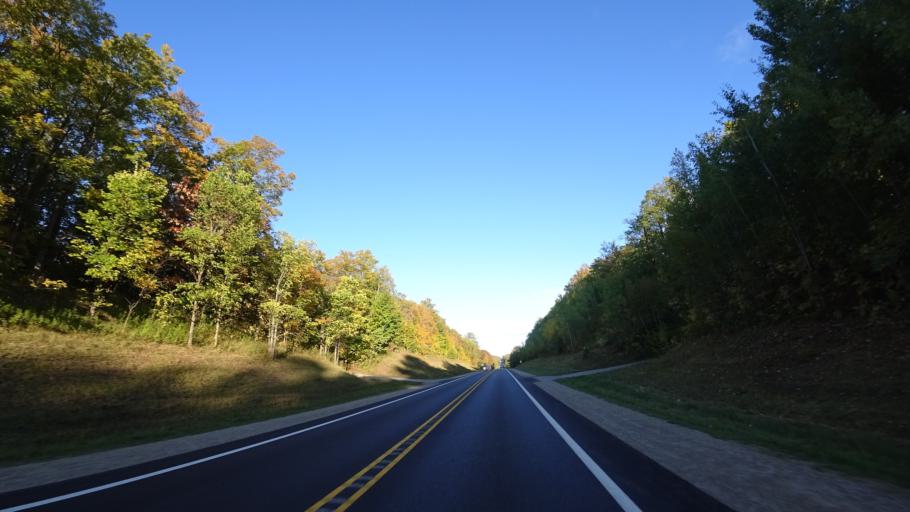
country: US
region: Michigan
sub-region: Luce County
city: Newberry
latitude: 46.3356
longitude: -85.8062
